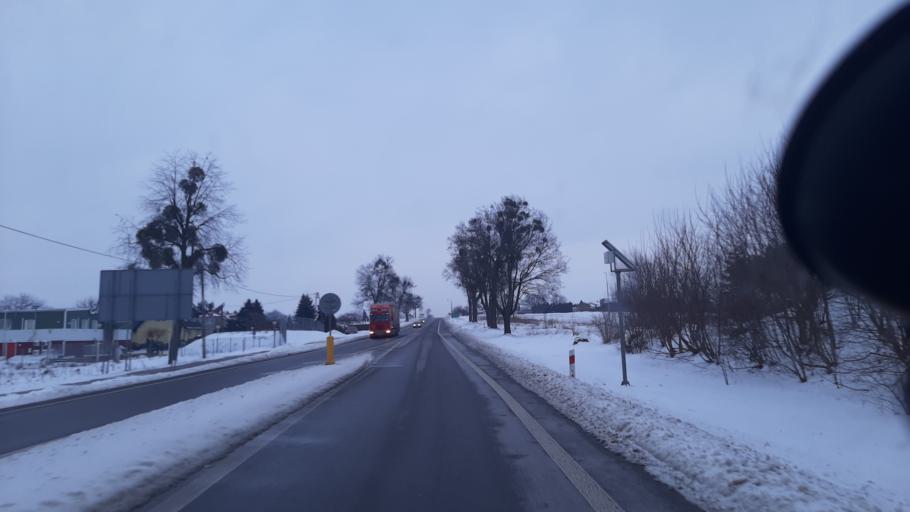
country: PL
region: Lublin Voivodeship
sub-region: Powiat pulawski
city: Markuszow
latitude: 51.3708
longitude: 22.2758
